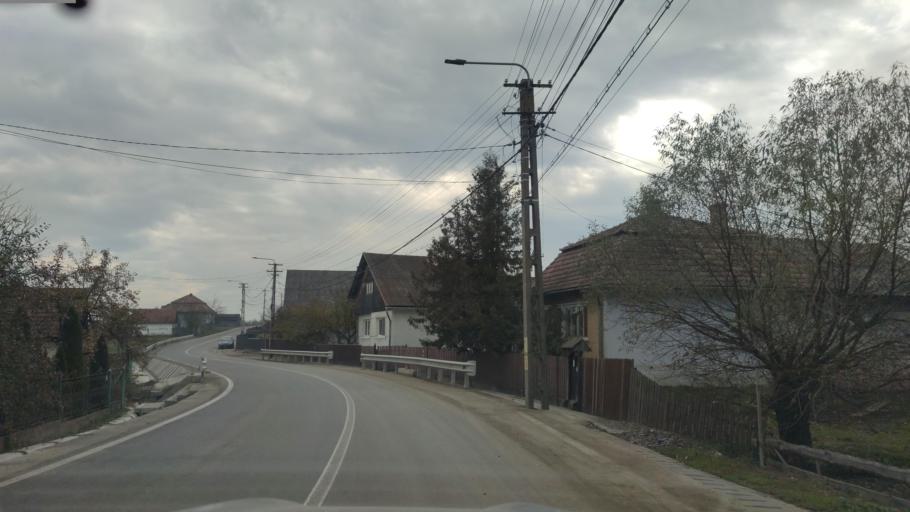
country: RO
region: Harghita
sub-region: Comuna Remetea
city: Remetea
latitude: 46.8110
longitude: 25.4592
